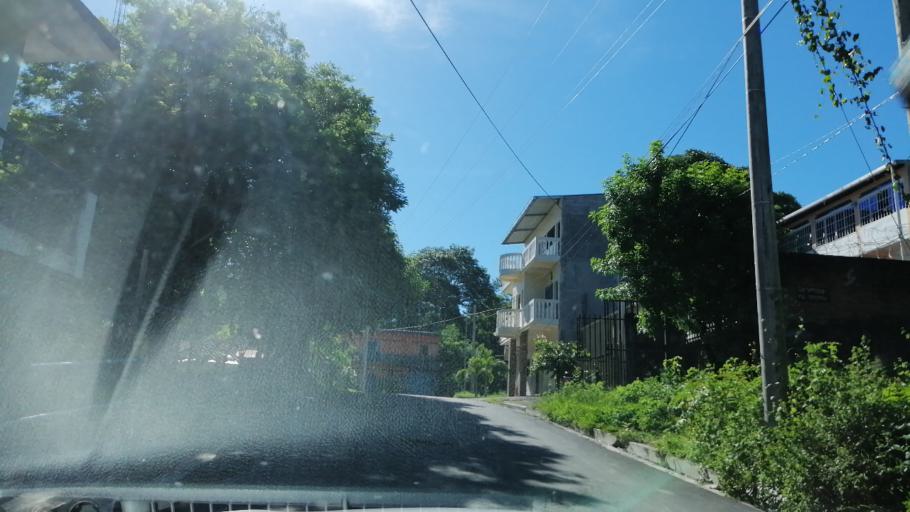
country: SV
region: Morazan
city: Corinto
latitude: 13.8055
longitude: -87.9685
